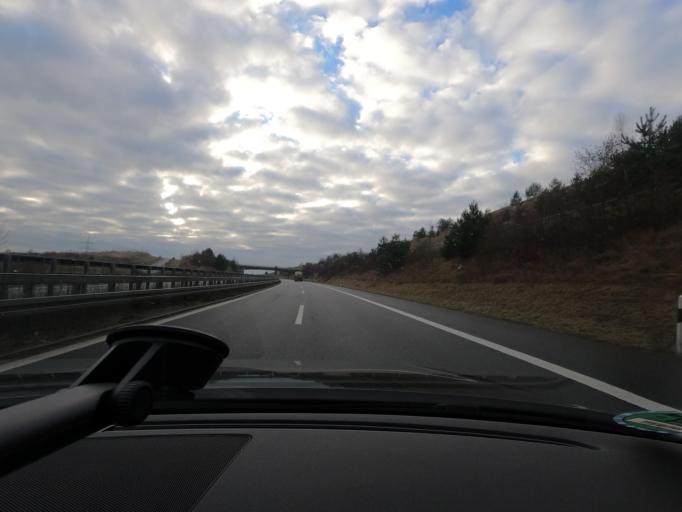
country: DE
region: Bavaria
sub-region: Upper Franconia
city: Rodental
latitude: 50.2636
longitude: 11.0173
